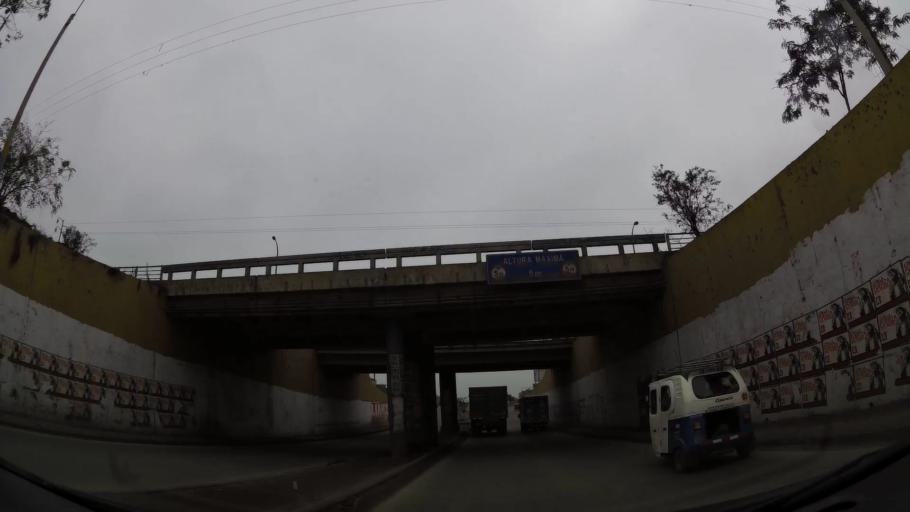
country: PE
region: Lima
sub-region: Lima
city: Surco
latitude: -12.2050
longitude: -76.9343
